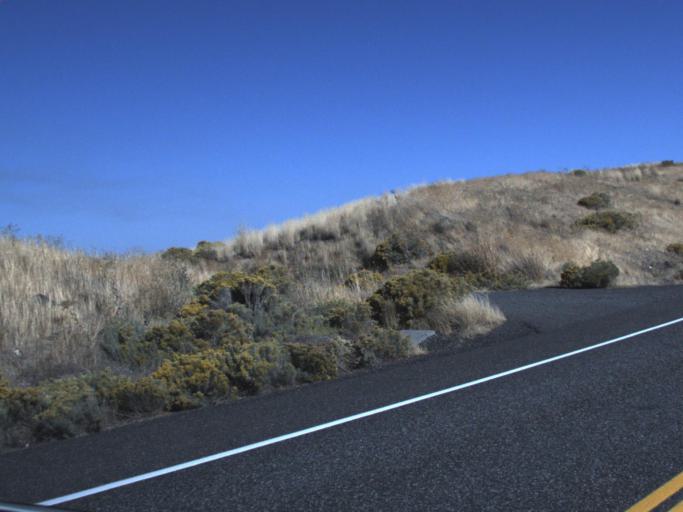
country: US
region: Washington
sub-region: Benton County
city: Highland
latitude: 46.1330
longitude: -119.0873
